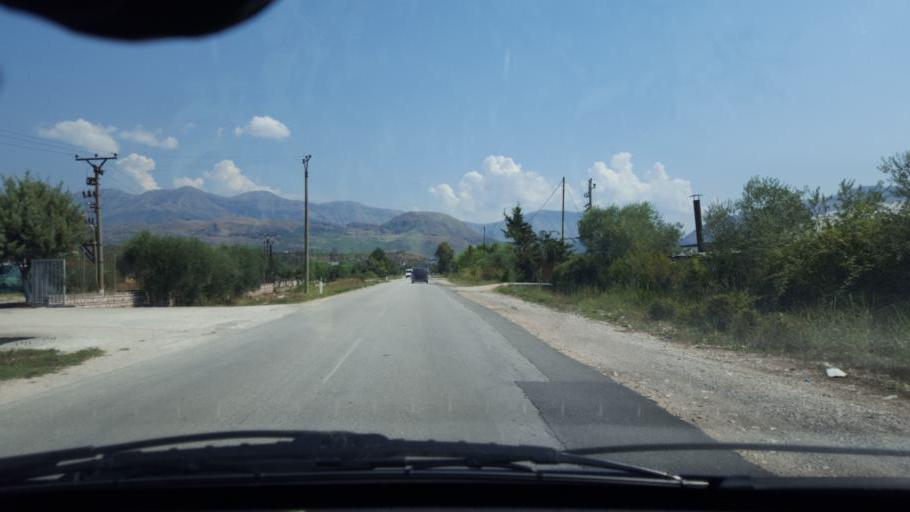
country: AL
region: Vlore
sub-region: Rrethi i Delvines
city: Finiq
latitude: 39.8920
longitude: 20.0669
